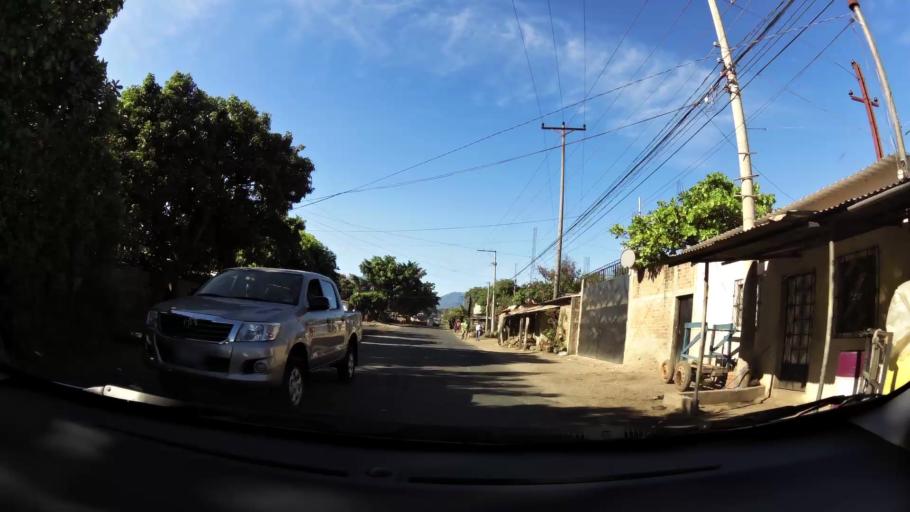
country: SV
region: Santa Ana
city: Santa Ana
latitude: 13.9777
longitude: -89.5807
